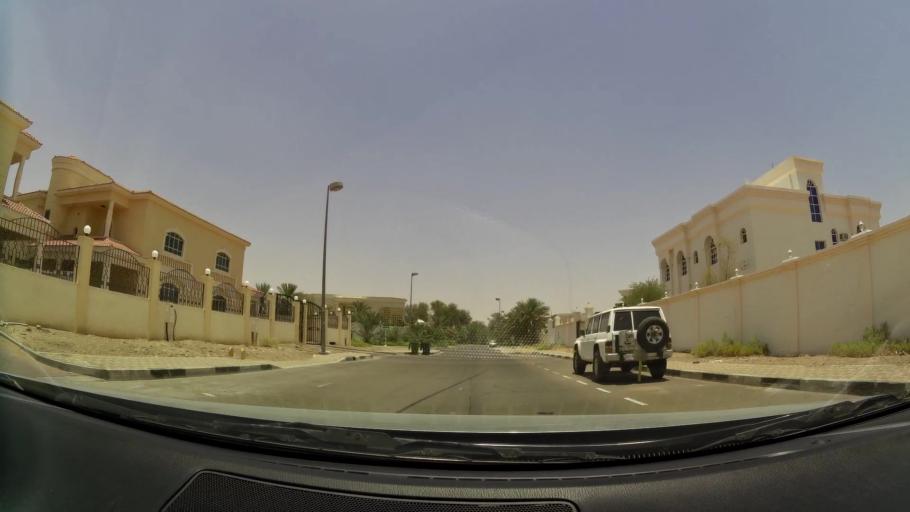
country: OM
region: Al Buraimi
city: Al Buraymi
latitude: 24.2722
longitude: 55.7275
